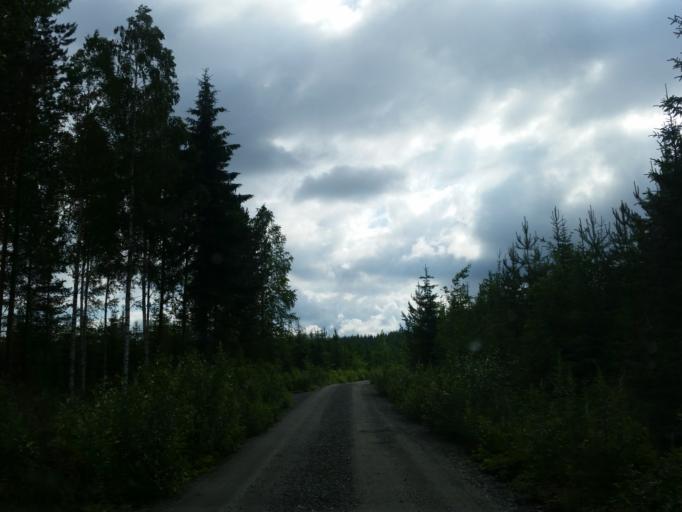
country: FI
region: Northern Savo
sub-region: Sisae-Savo
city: Tervo
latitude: 63.0562
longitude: 26.6709
